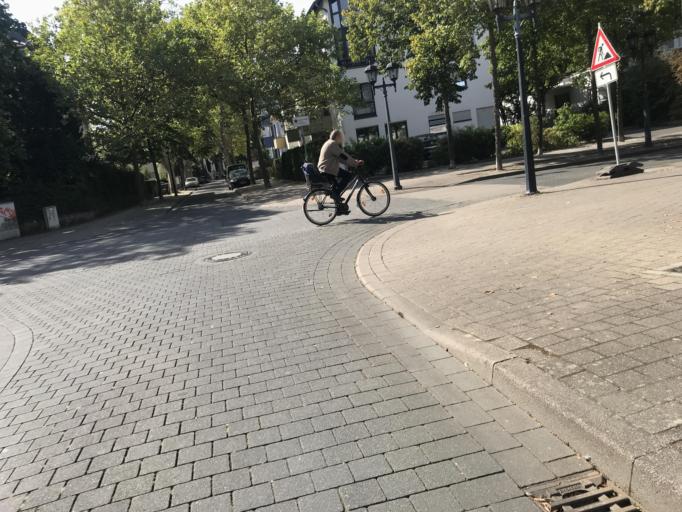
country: DE
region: Rheinland-Pfalz
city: Bad Kreuznach
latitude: 49.8397
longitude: 7.8564
